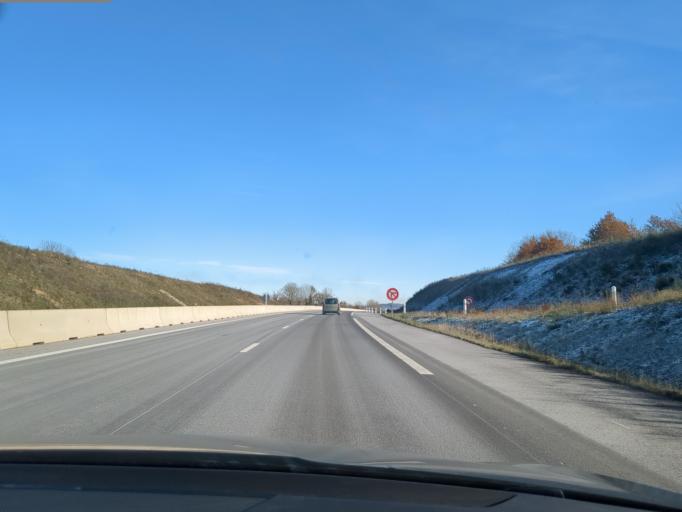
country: FR
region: Auvergne
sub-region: Departement de l'Allier
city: Buxieres-les-Mines
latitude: 46.3992
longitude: 3.0474
